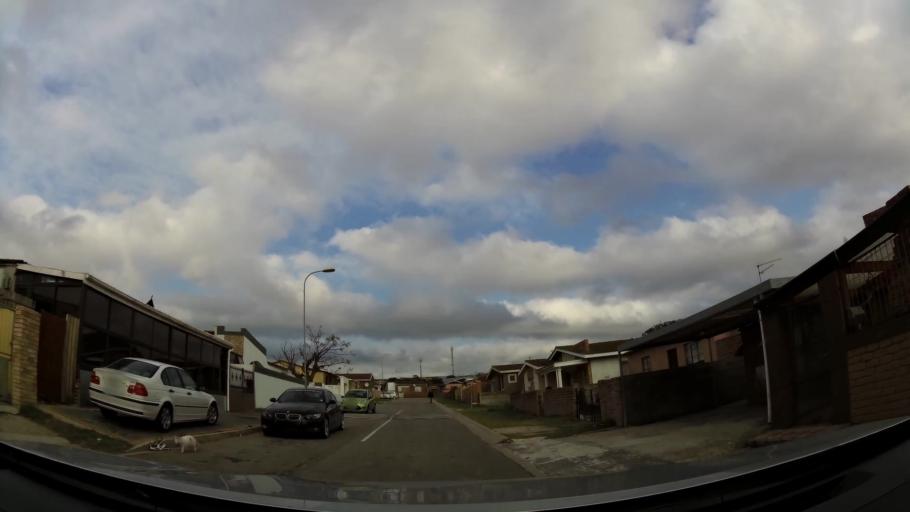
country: ZA
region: Eastern Cape
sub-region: Nelson Mandela Bay Metropolitan Municipality
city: Port Elizabeth
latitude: -33.9166
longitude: 25.5527
